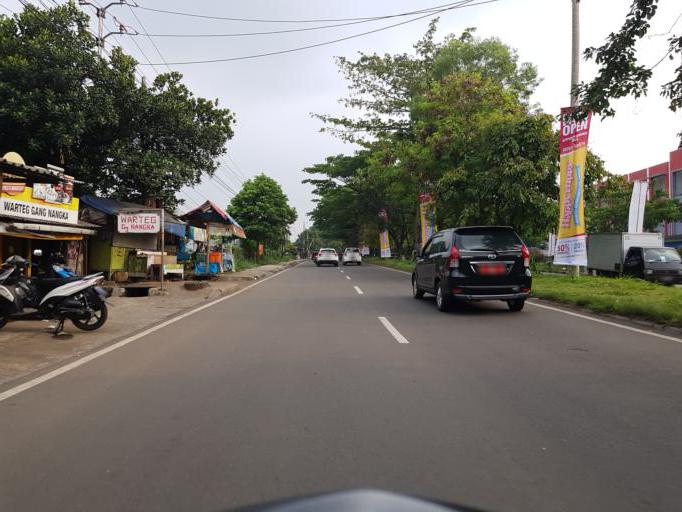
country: ID
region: West Java
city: Bogor
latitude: -6.5476
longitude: 106.7745
